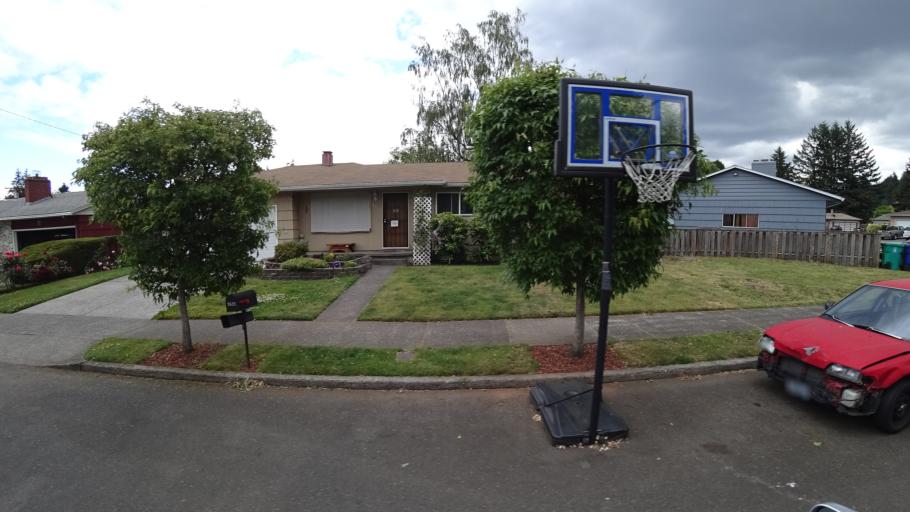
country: US
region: Oregon
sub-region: Clackamas County
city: Happy Valley
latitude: 45.4970
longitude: -122.5008
